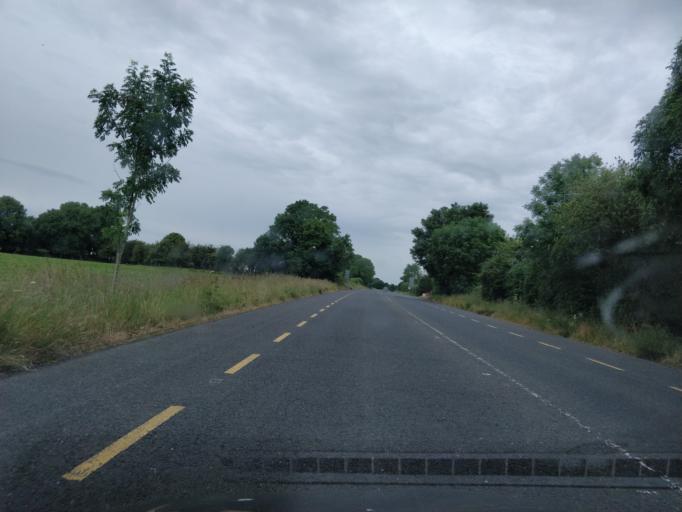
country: IE
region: Munster
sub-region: North Tipperary
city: Roscrea
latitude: 52.9511
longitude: -7.6888
